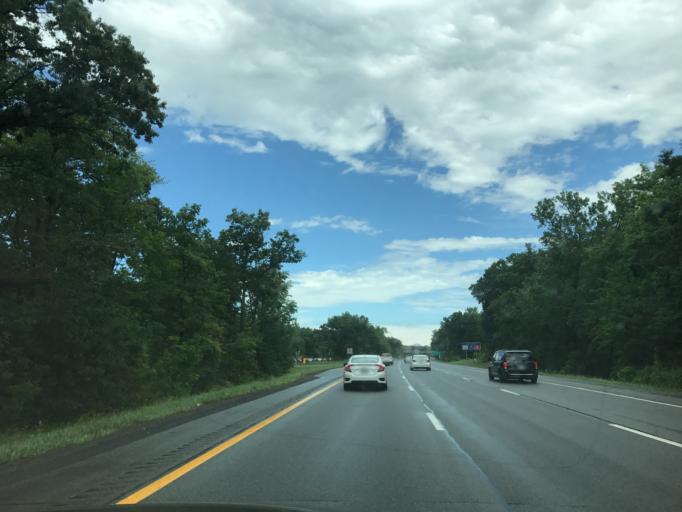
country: US
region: New York
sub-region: Albany County
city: Cohoes
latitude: 42.8123
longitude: -73.7665
